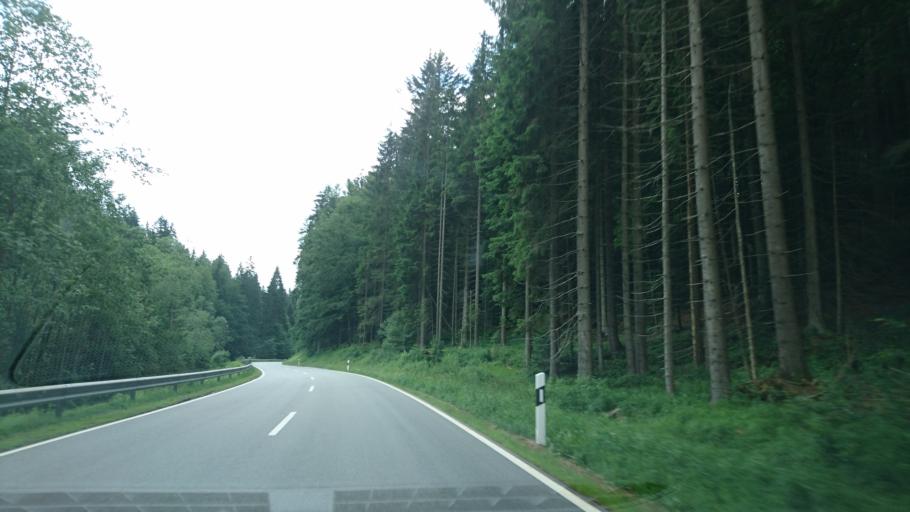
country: DE
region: Bavaria
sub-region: Lower Bavaria
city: Mauth
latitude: 48.8811
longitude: 13.5744
